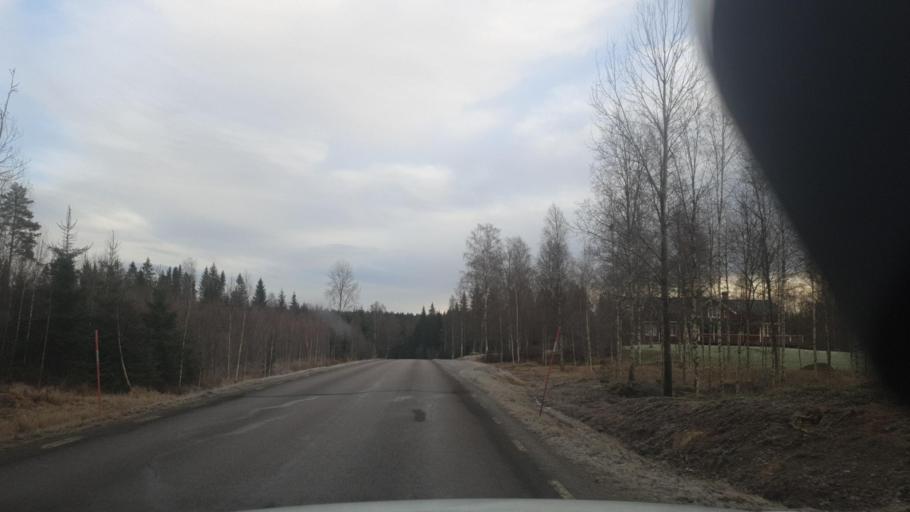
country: SE
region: Vaermland
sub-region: Eda Kommun
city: Charlottenberg
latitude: 59.8707
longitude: 12.4048
